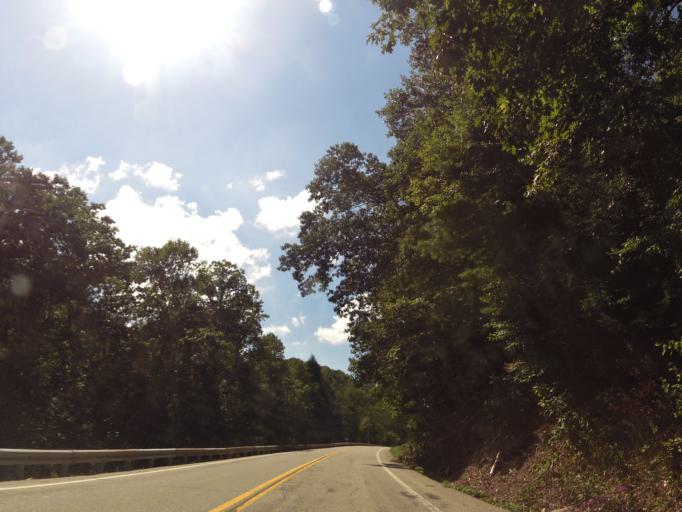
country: US
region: Tennessee
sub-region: Cumberland County
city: Fairfield Glade
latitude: 35.8843
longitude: -84.8280
